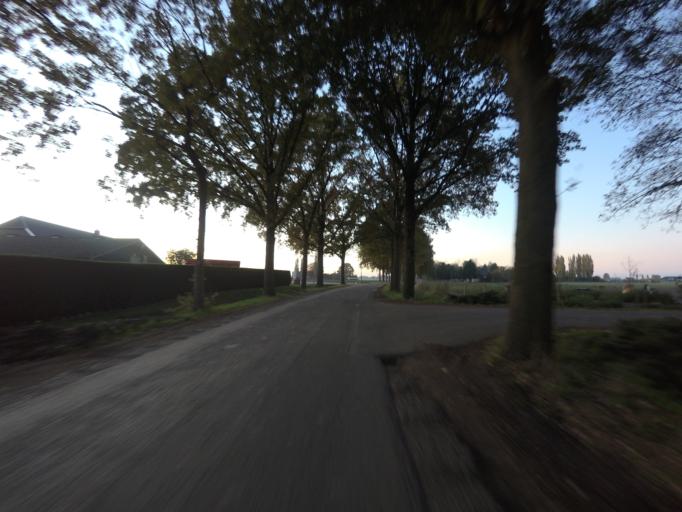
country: NL
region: North Brabant
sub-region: Gemeente Woudrichem
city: Almkerk
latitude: 51.7816
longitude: 4.9606
